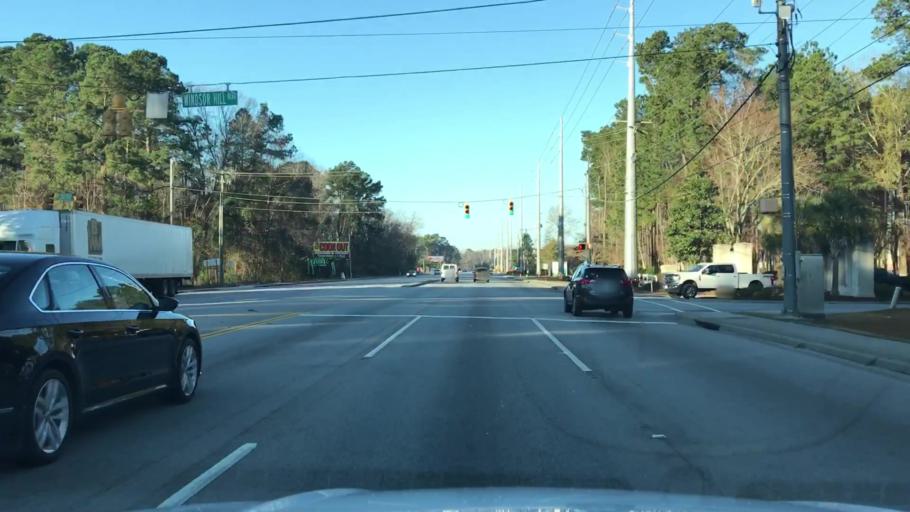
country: US
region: South Carolina
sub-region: Berkeley County
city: Ladson
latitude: 32.9239
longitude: -80.0891
